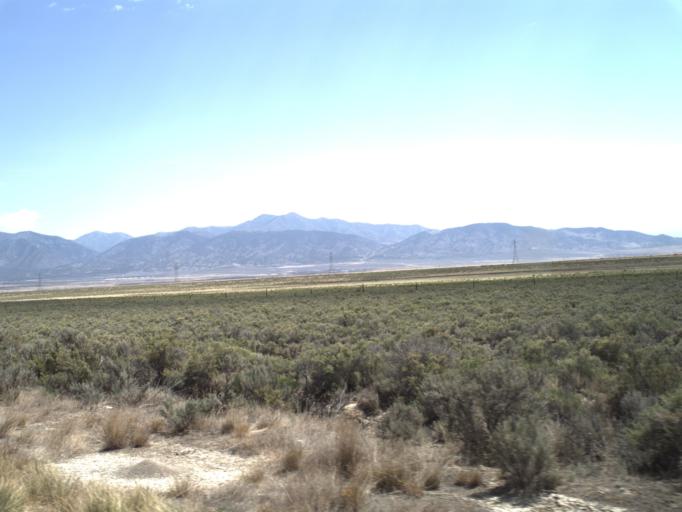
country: US
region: Utah
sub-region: Tooele County
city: Tooele
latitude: 40.2253
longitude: -112.4043
